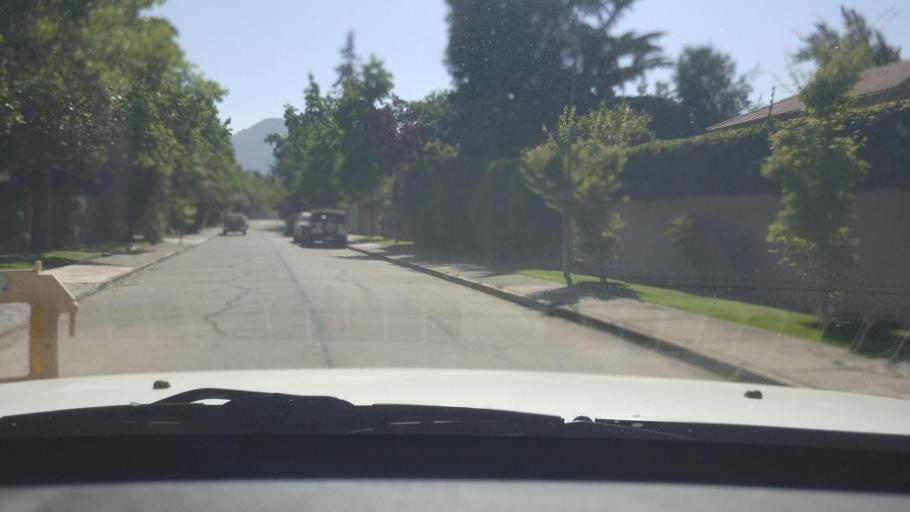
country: CL
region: Santiago Metropolitan
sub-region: Provincia de Santiago
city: Villa Presidente Frei, Nunoa, Santiago, Chile
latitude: -33.3750
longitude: -70.5127
